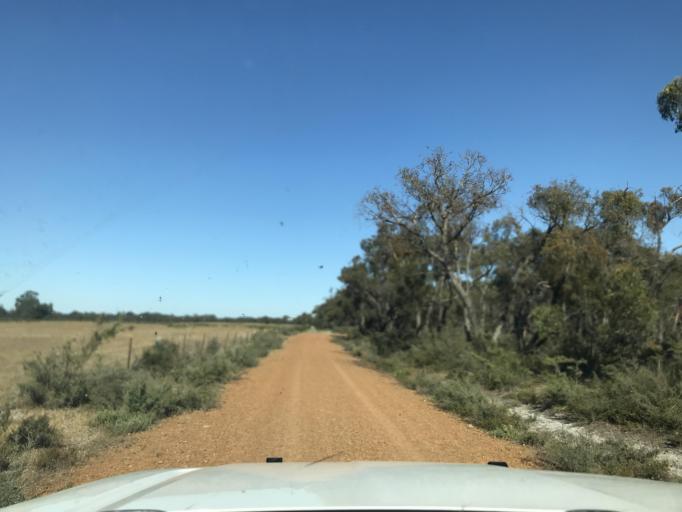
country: AU
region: South Australia
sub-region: Wattle Range
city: Penola
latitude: -37.0819
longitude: 141.3976
